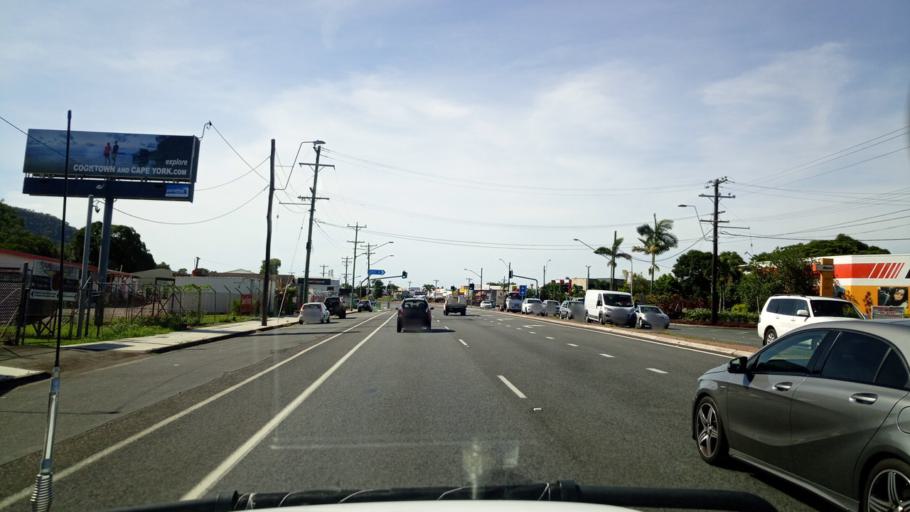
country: AU
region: Queensland
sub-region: Cairns
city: Cairns
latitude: -16.8984
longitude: 145.7553
